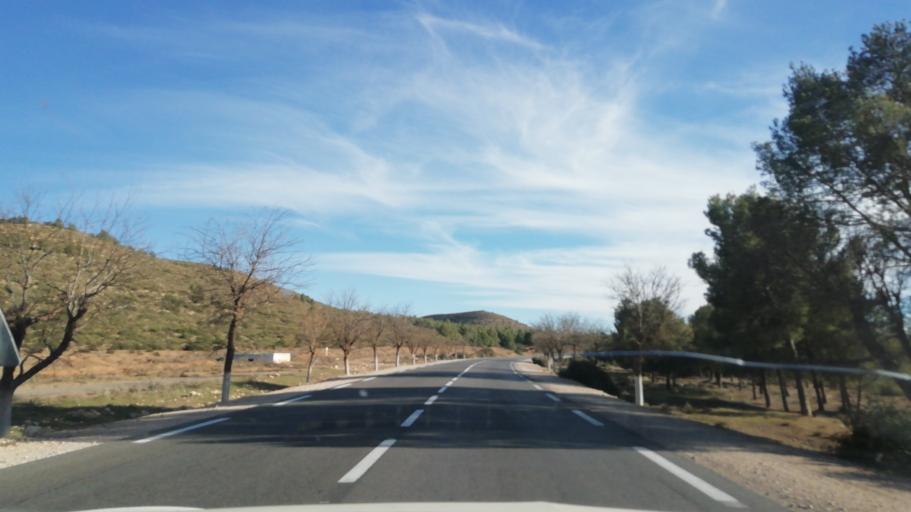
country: DZ
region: Tlemcen
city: Sebdou
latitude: 34.5953
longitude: -1.3213
